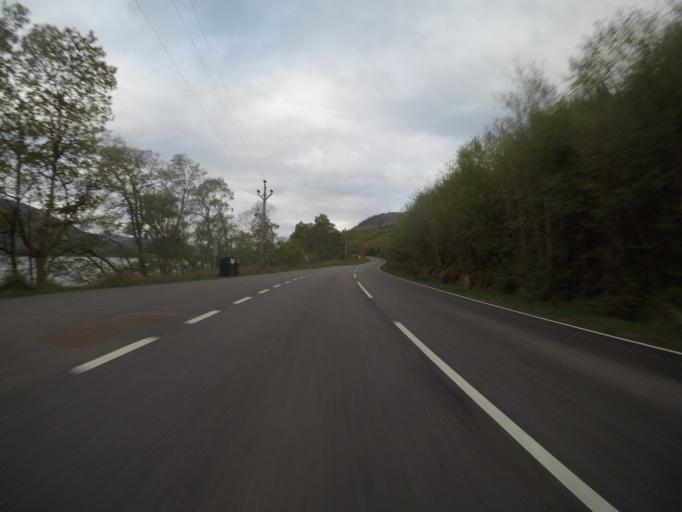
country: GB
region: Scotland
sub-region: Highland
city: Beauly
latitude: 57.1797
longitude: -4.6343
